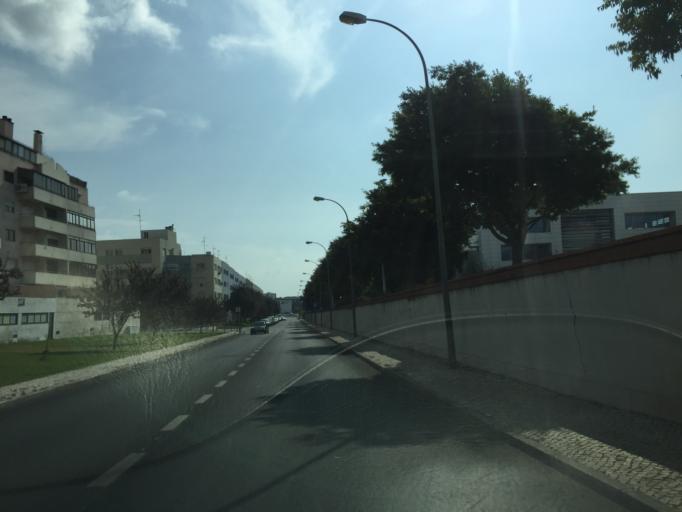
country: PT
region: Lisbon
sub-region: Odivelas
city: Pontinha
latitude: 38.7687
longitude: -9.1800
